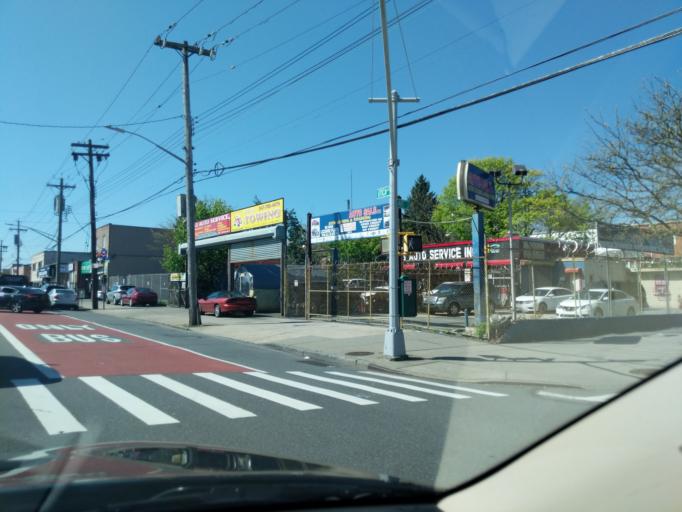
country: US
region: New York
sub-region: Kings County
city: Brooklyn
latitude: 40.6282
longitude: -73.9278
